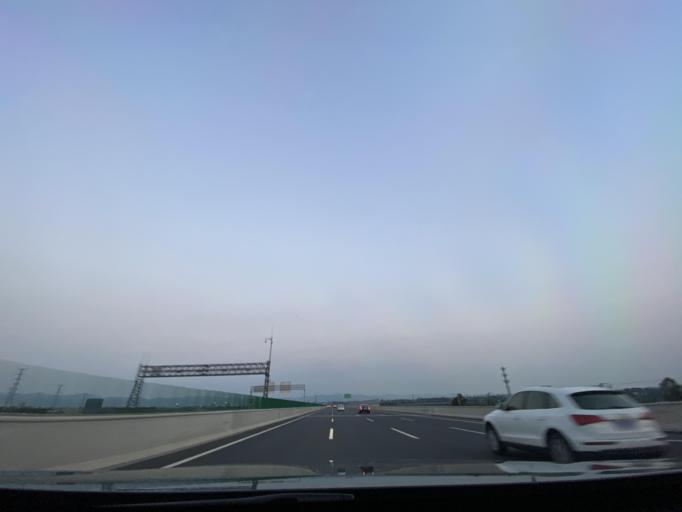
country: CN
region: Sichuan
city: Longquan
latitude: 30.5519
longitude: 104.1489
